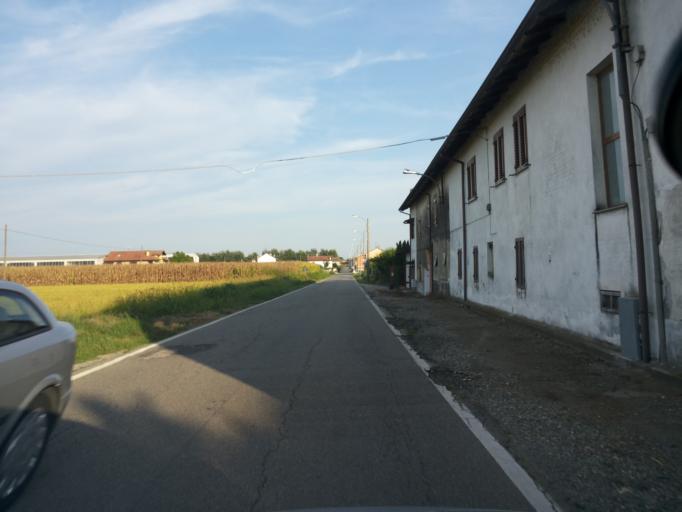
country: IT
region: Piedmont
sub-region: Provincia di Vercelli
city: Crova
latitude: 45.3339
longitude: 8.2023
